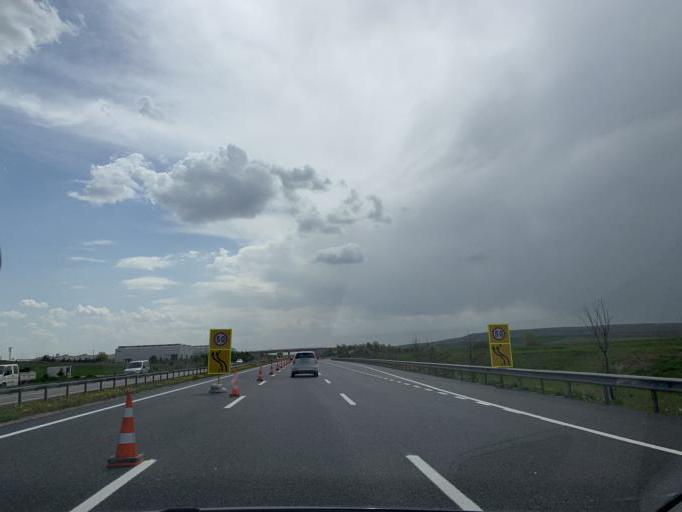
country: TR
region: Ankara
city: Polatli
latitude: 39.6545
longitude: 32.2167
